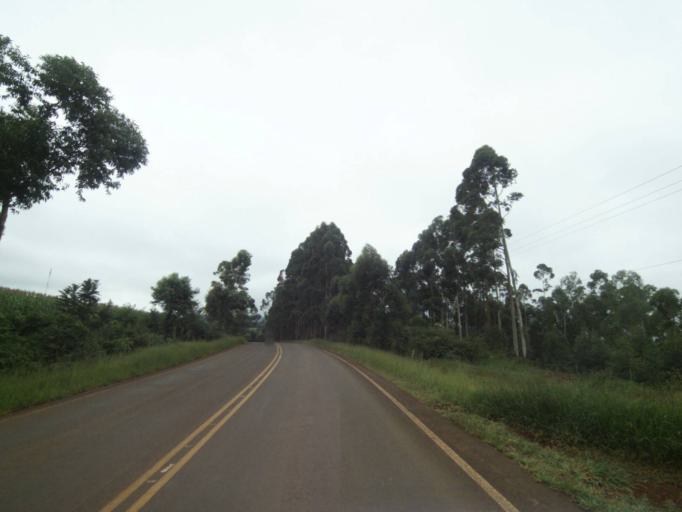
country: BR
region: Parana
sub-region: Pitanga
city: Pitanga
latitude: -24.9139
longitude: -51.8701
